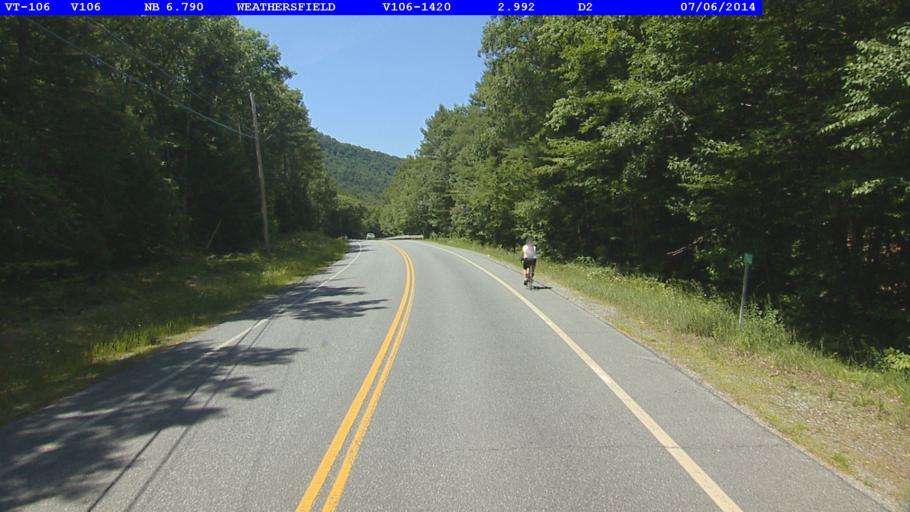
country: US
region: Vermont
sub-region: Windsor County
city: Springfield
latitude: 43.3824
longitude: -72.5098
